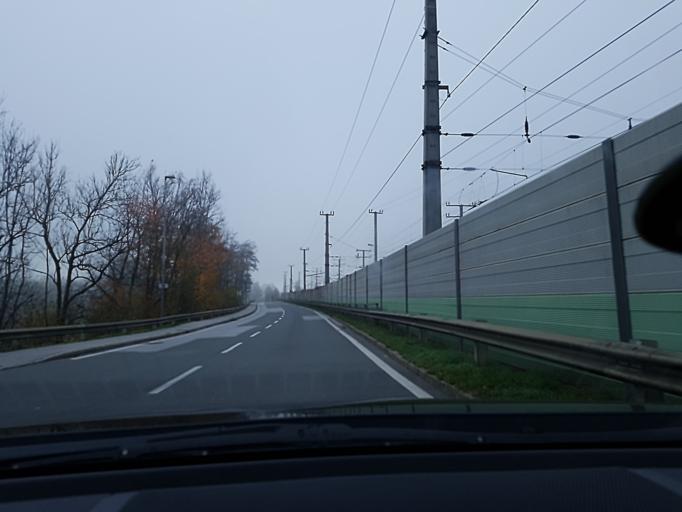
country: AT
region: Salzburg
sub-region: Politischer Bezirk Sankt Johann im Pongau
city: Sankt Johann im Pongau
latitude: 47.3466
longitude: 13.1949
